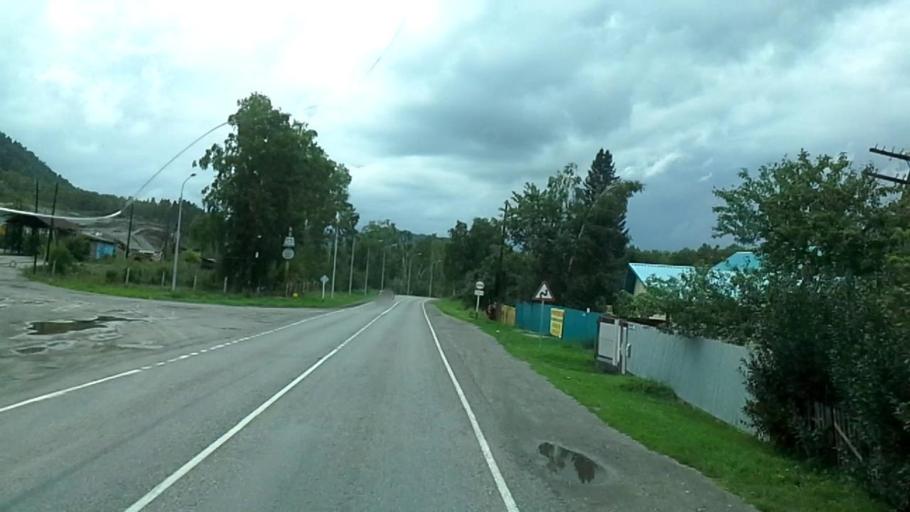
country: RU
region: Altay
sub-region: Mayminskiy Rayon
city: Manzherok
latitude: 51.8696
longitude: 85.7814
